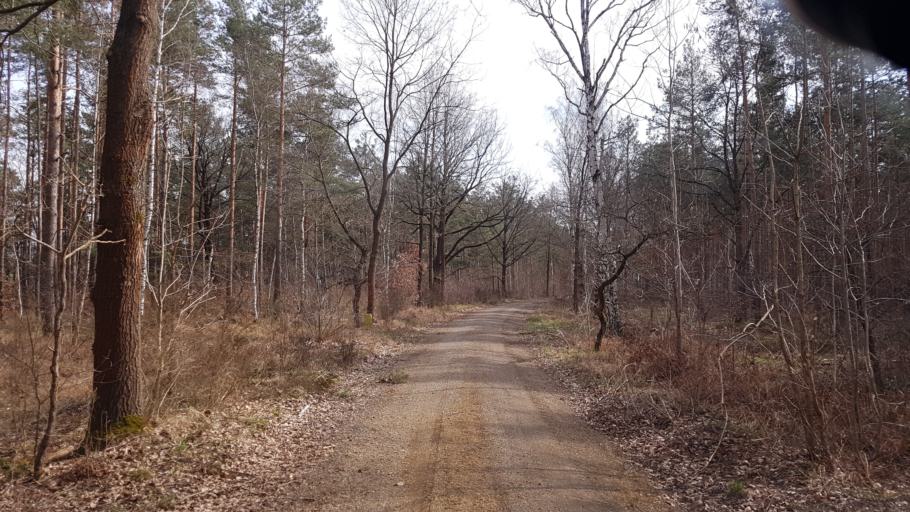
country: DE
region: Brandenburg
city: Lauchhammer
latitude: 51.5317
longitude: 13.7084
